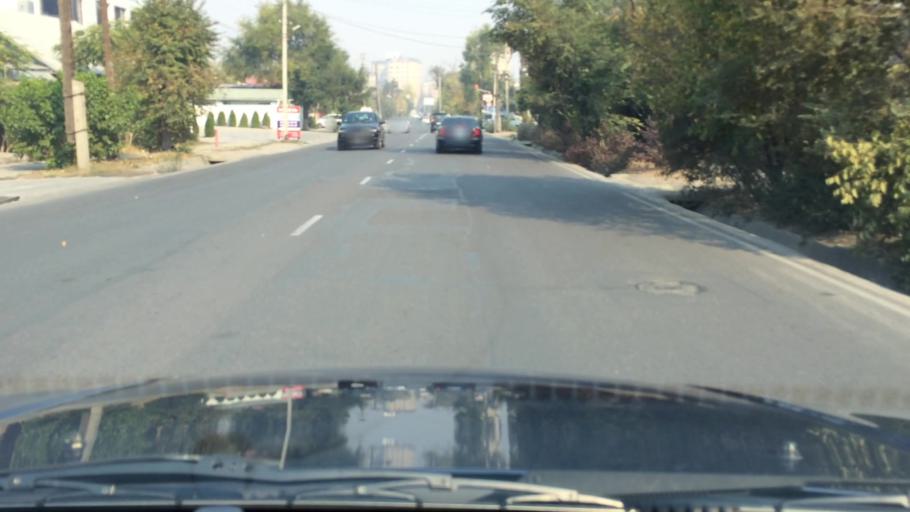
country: KG
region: Chuy
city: Bishkek
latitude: 42.8589
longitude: 74.5999
